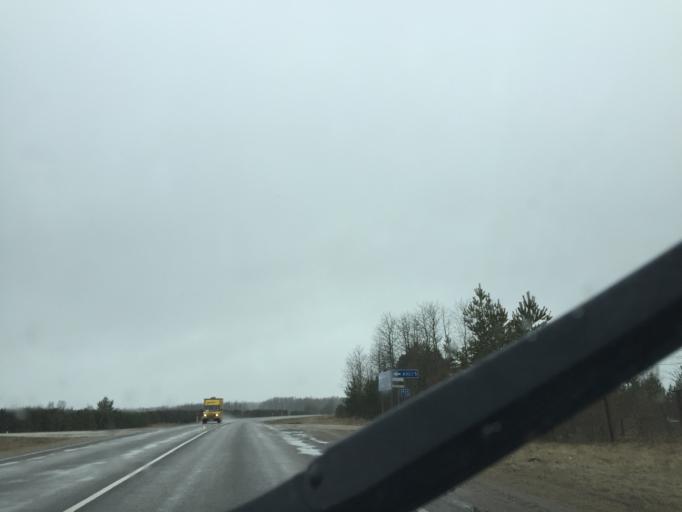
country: EE
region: Laeaene
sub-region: Ridala Parish
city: Uuemoisa
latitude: 58.8809
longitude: 23.6042
